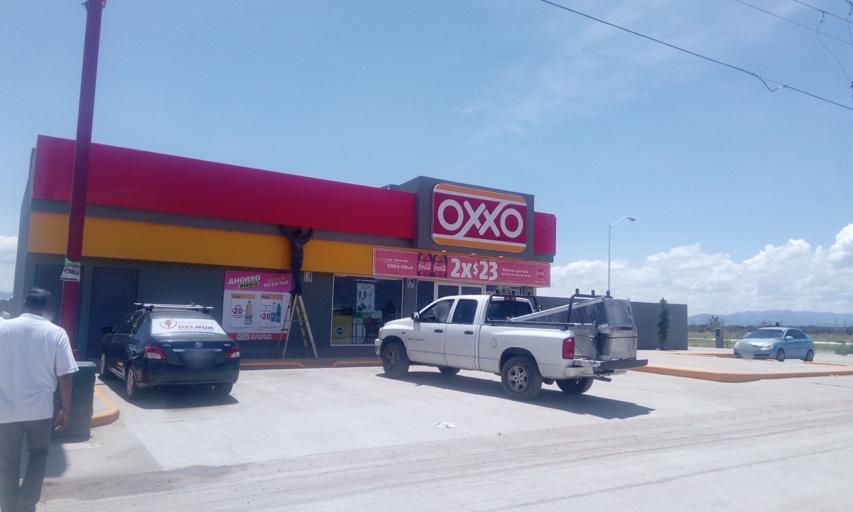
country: MX
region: Durango
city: Victoria de Durango
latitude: 24.0130
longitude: -104.5951
